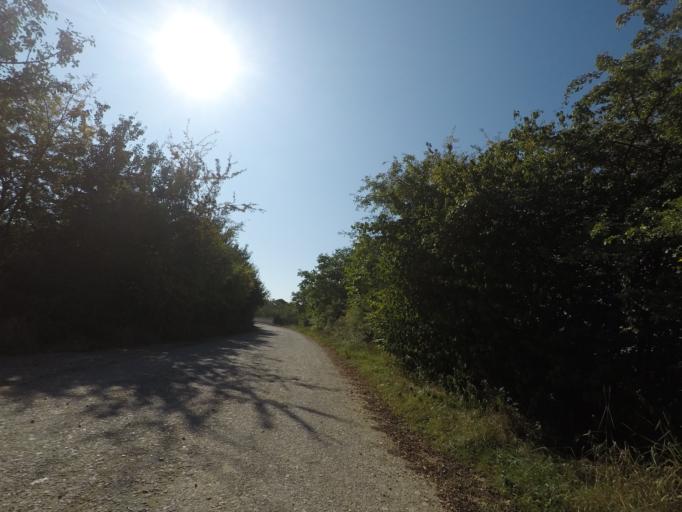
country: LU
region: Luxembourg
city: Itzig
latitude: 49.6125
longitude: 6.1760
